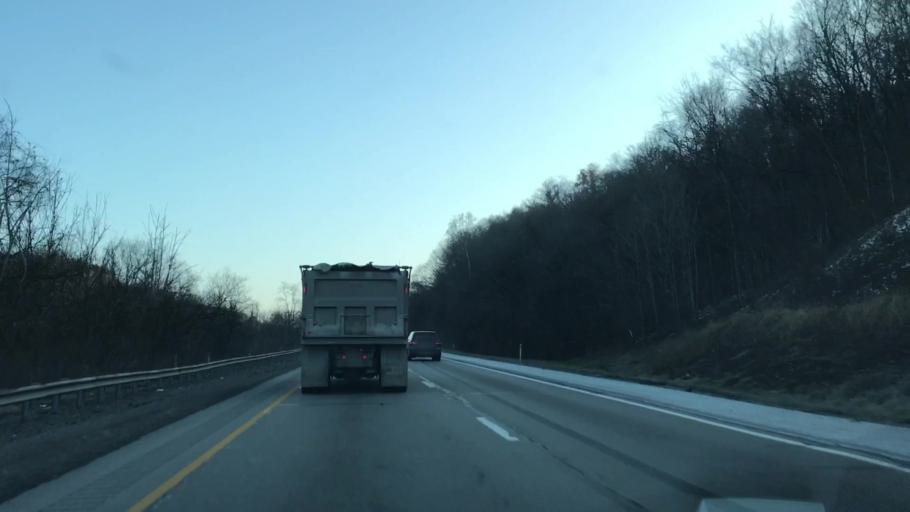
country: US
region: Pennsylvania
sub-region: Allegheny County
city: Emsworth
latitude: 40.4872
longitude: -80.1250
